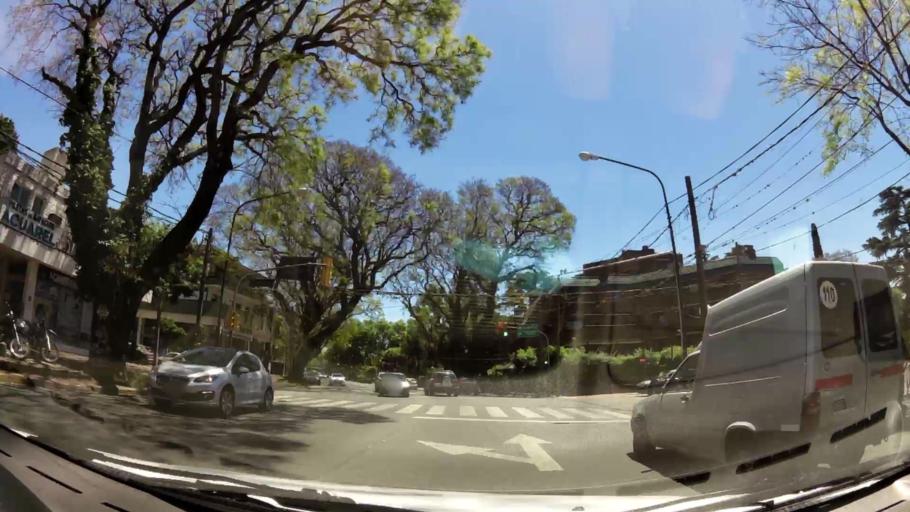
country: AR
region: Buenos Aires
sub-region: Partido de San Isidro
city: San Isidro
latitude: -34.4793
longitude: -58.4935
